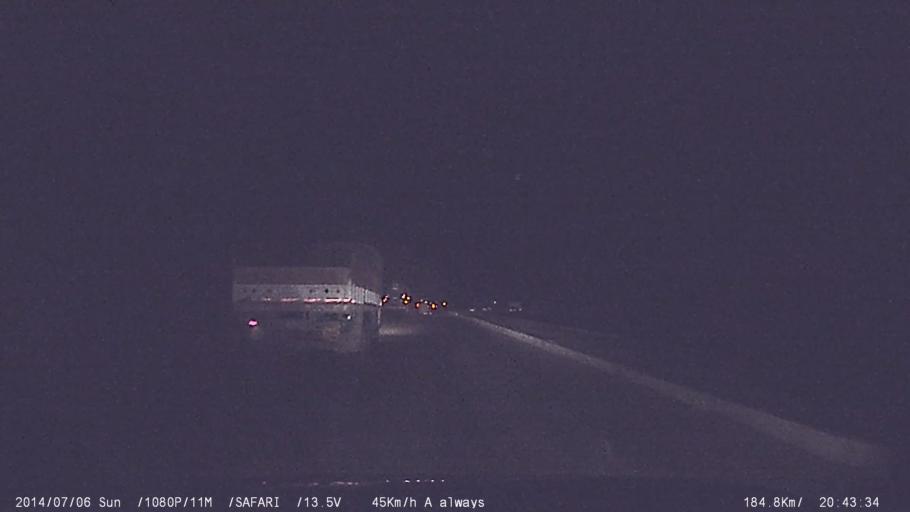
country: IN
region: Tamil Nadu
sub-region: Coimbatore
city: Madukkarai
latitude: 10.8497
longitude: 76.8407
